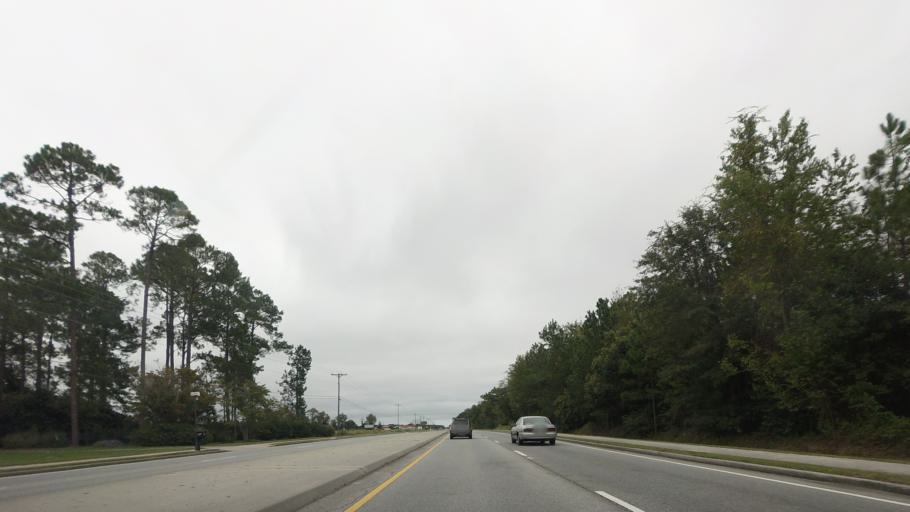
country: US
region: Georgia
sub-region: Berrien County
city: Ray City
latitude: 30.9545
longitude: -83.2264
